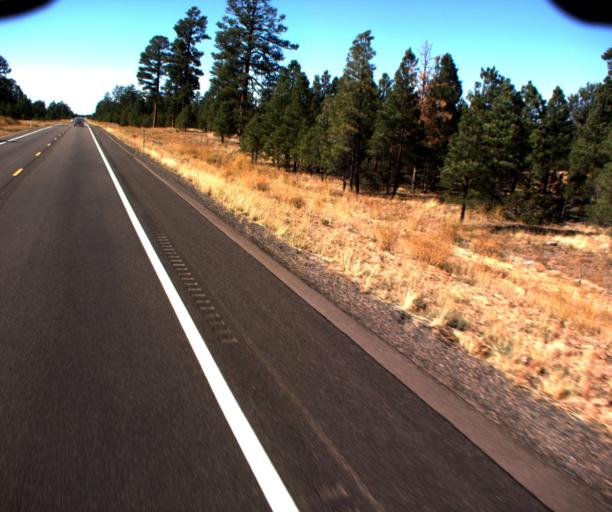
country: US
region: Arizona
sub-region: Apache County
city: Saint Michaels
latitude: 35.6979
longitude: -109.2808
